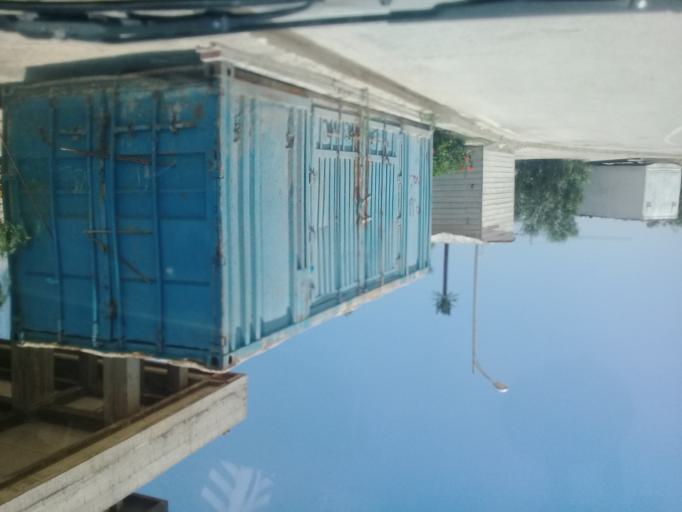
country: TN
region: Tunis
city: La Goulette
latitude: 36.8424
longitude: 10.2787
